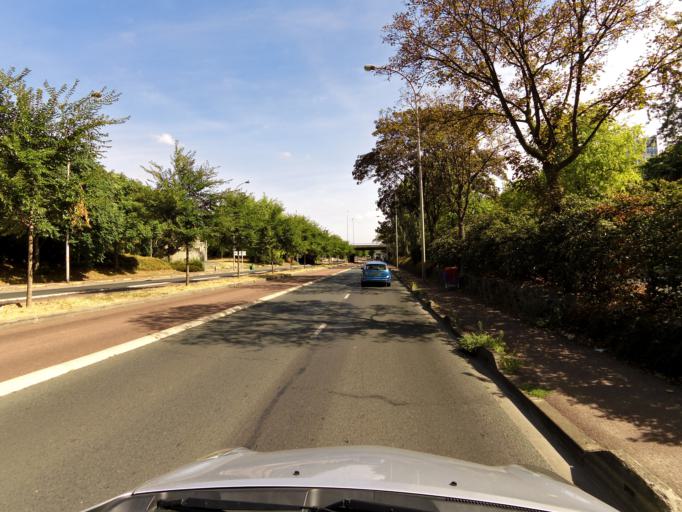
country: FR
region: Ile-de-France
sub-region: Departement du Val-de-Marne
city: Creteil
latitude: 48.7848
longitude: 2.4483
